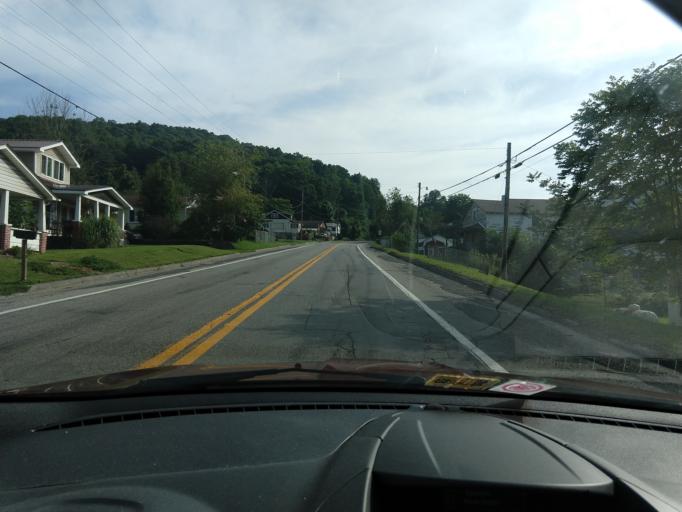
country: US
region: West Virginia
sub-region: Greenbrier County
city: Rainelle
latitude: 38.0045
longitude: -80.7352
